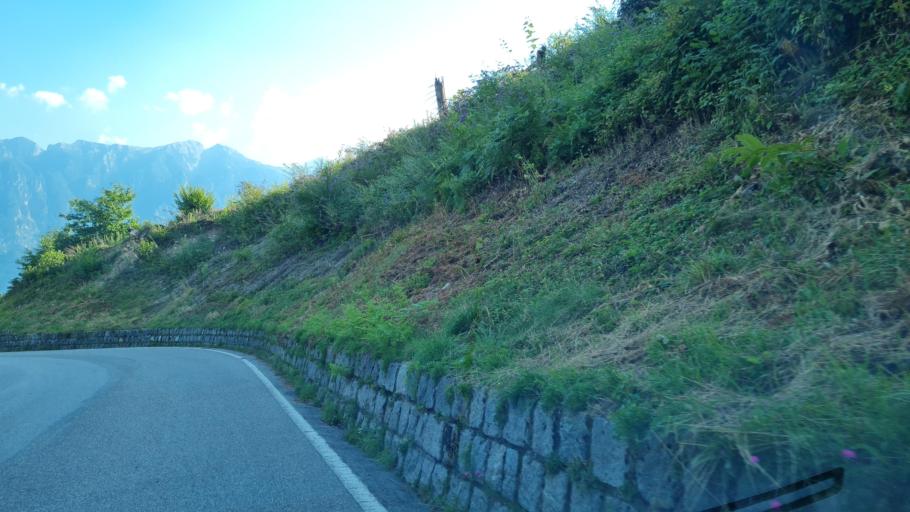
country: IT
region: Trentino-Alto Adige
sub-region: Provincia di Trento
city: Carzano
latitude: 46.0943
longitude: 11.4985
